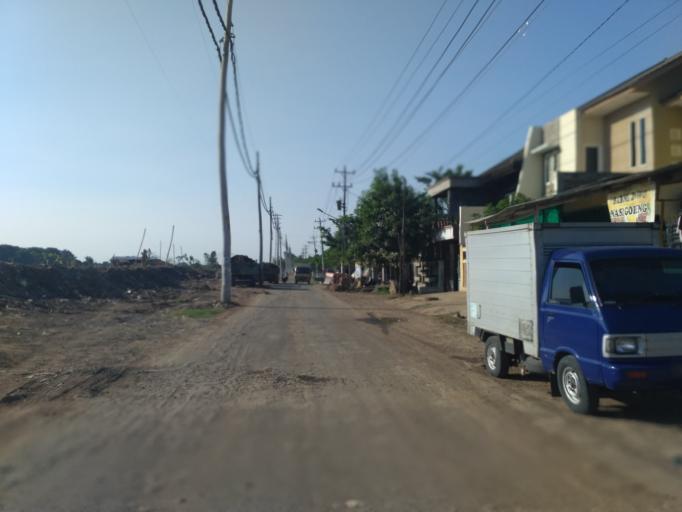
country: ID
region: Central Java
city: Semarang
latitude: -6.9905
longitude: 110.4407
